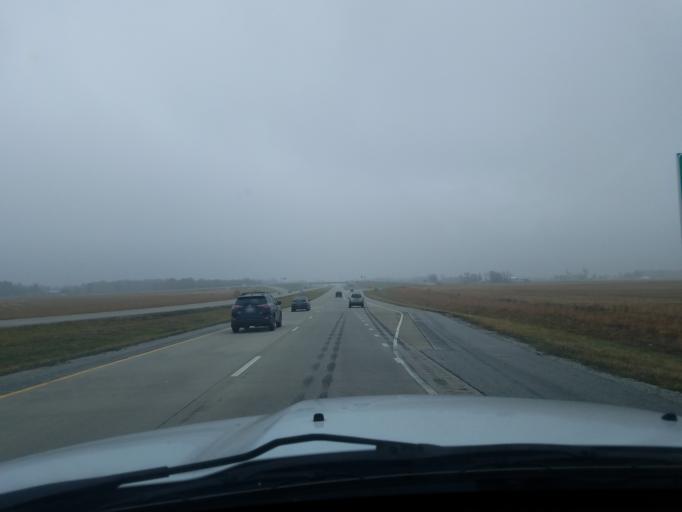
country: US
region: Indiana
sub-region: Howard County
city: Indian Heights
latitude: 40.4132
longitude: -86.0974
